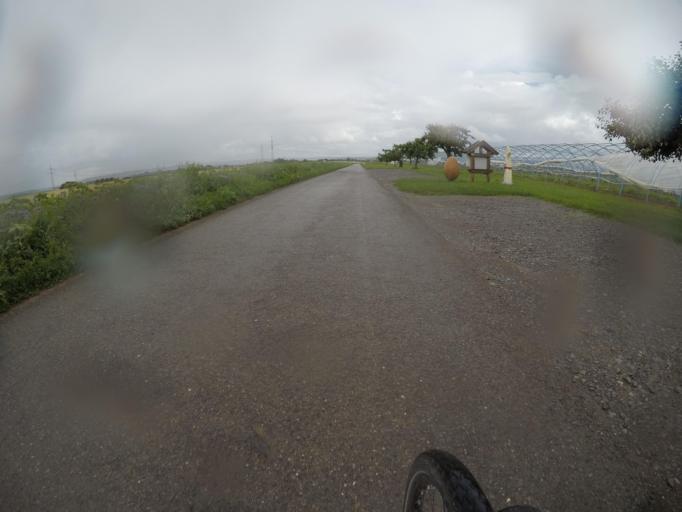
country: DE
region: Baden-Wuerttemberg
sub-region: Regierungsbezirk Stuttgart
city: Bondorf
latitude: 48.5128
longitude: 8.8103
